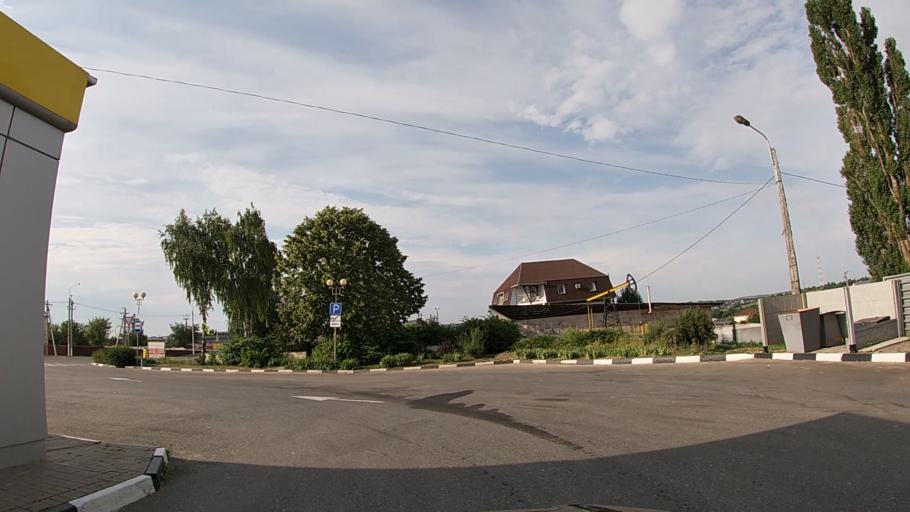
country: RU
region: Belgorod
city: Severnyy
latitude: 50.6421
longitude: 36.4682
